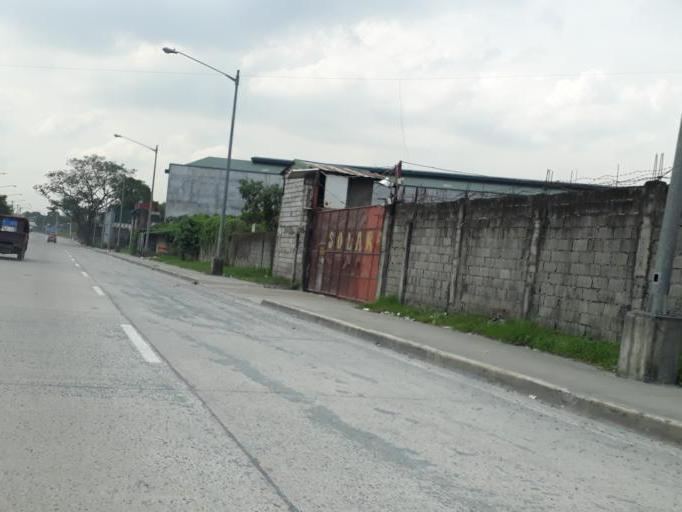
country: PH
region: Calabarzon
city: Bagong Pagasa
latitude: 14.7024
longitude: 121.0149
